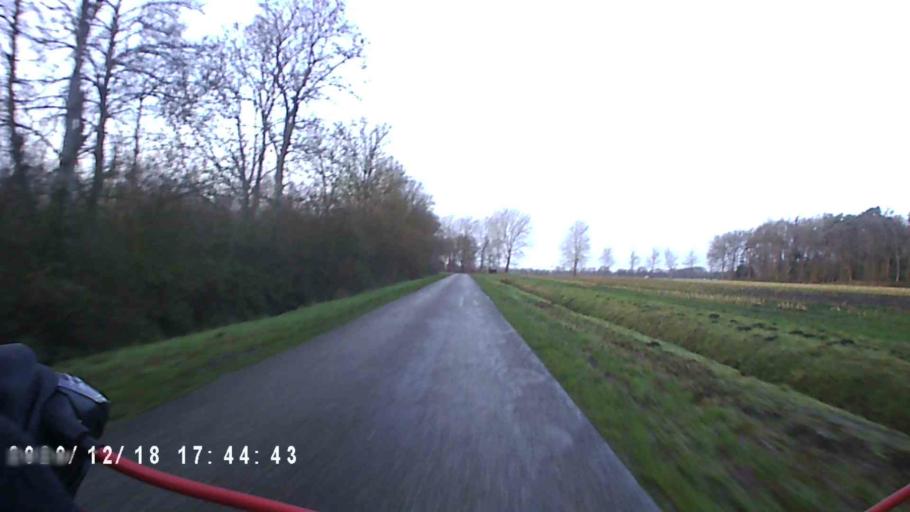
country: NL
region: Drenthe
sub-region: Gemeente Tynaarlo
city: Vries
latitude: 53.1084
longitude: 6.5680
